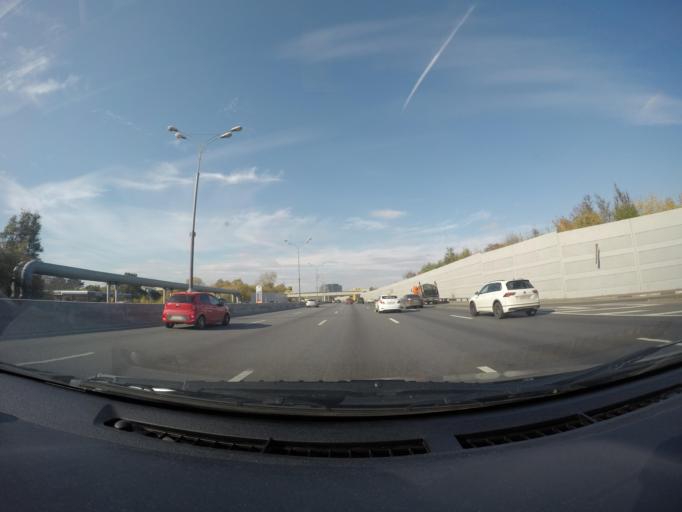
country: RU
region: Moscow
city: Yaroslavskiy
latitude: 55.8919
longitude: 37.7067
